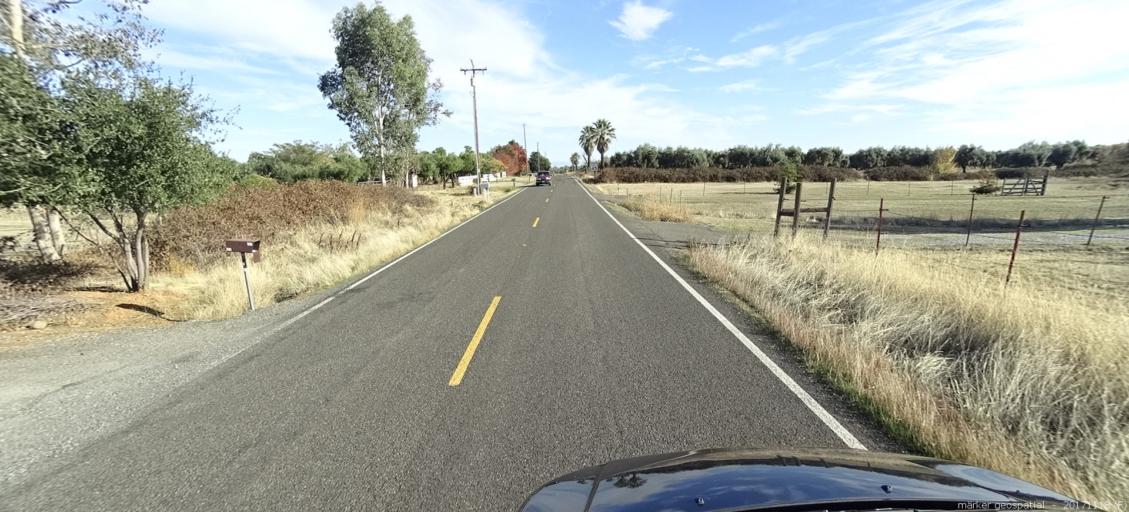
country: US
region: California
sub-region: Shasta County
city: Anderson
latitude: 40.4471
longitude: -122.4408
